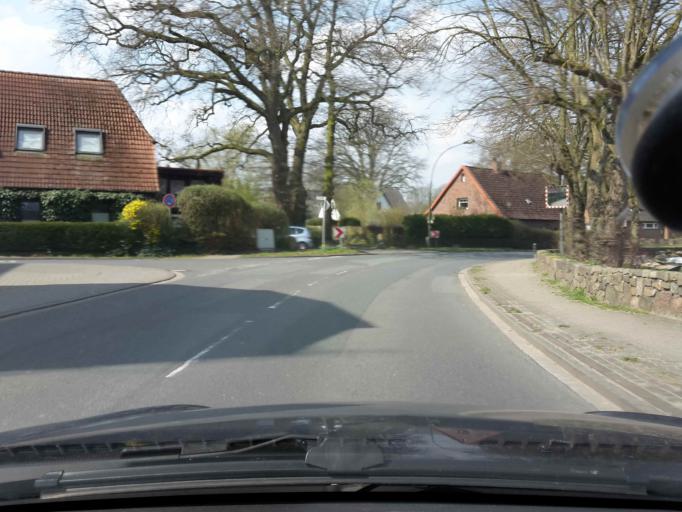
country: DE
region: Lower Saxony
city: Harmstorf
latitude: 53.3642
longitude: 9.9839
